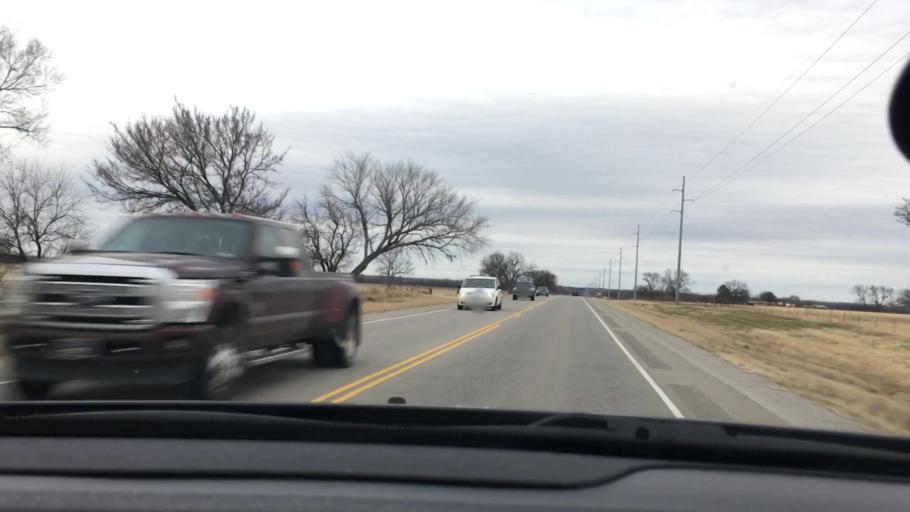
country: US
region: Oklahoma
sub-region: Marshall County
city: Oakland
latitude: 34.1945
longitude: -96.8022
